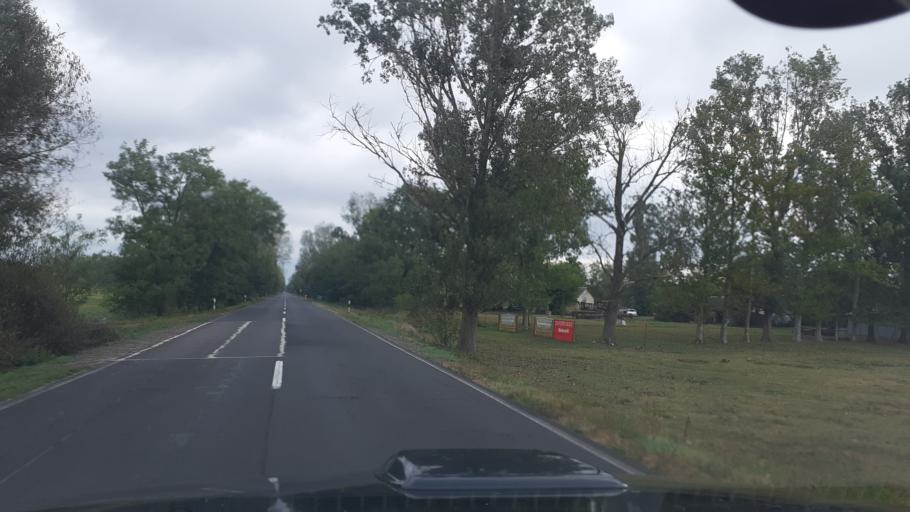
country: HU
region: Bacs-Kiskun
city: Agasegyhaza
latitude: 46.8766
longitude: 19.4798
